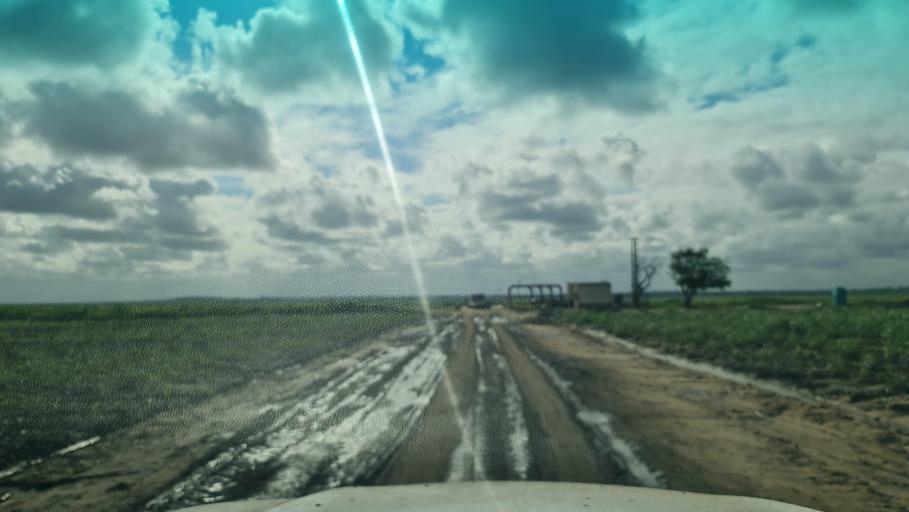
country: MZ
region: Maputo
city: Manhica
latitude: -25.4376
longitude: 32.8418
